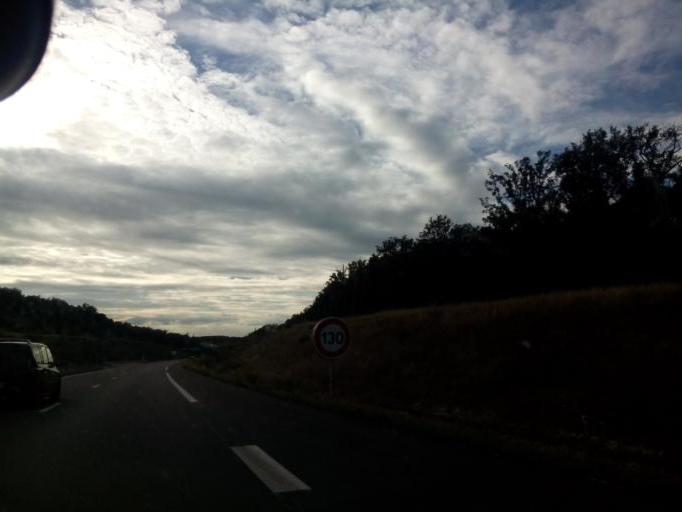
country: FR
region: Centre
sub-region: Departement d'Indre-et-Loire
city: Montbazon
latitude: 47.3026
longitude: 0.6838
